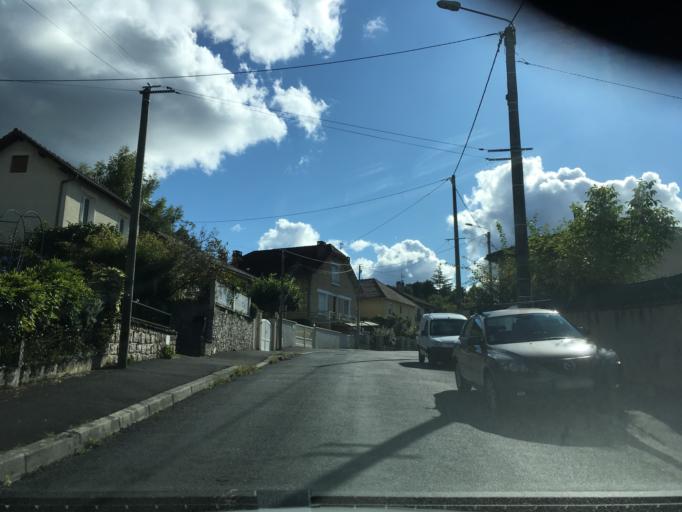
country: FR
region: Limousin
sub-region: Departement de la Correze
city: Brive-la-Gaillarde
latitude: 45.1458
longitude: 1.5007
